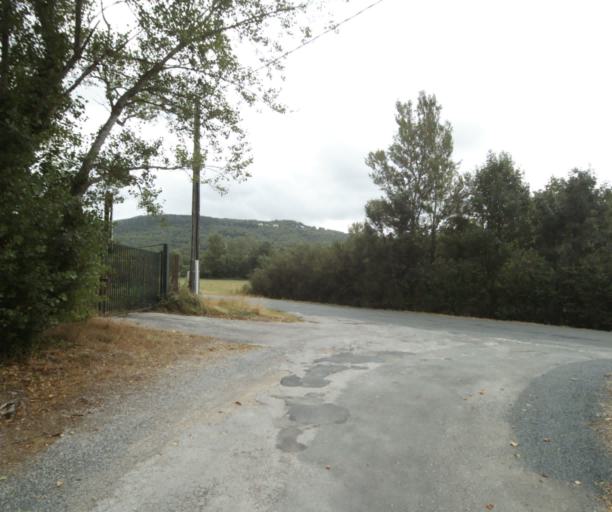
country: FR
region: Midi-Pyrenees
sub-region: Departement du Tarn
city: Soreze
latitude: 43.4492
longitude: 2.0512
